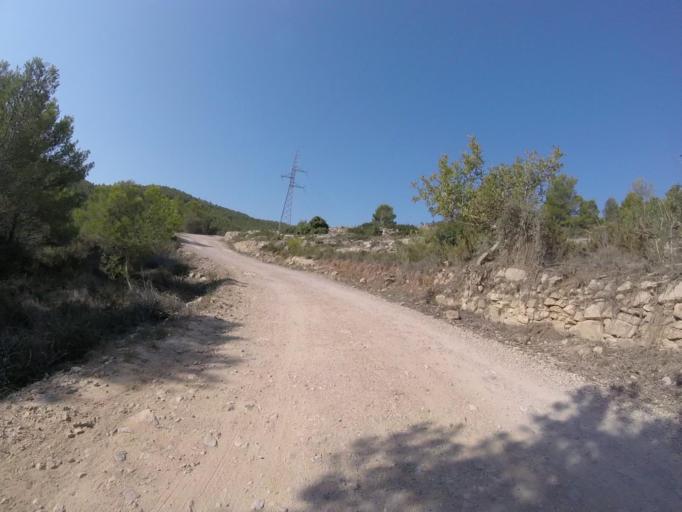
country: ES
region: Valencia
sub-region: Provincia de Castello
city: Peniscola
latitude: 40.3309
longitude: 0.3601
